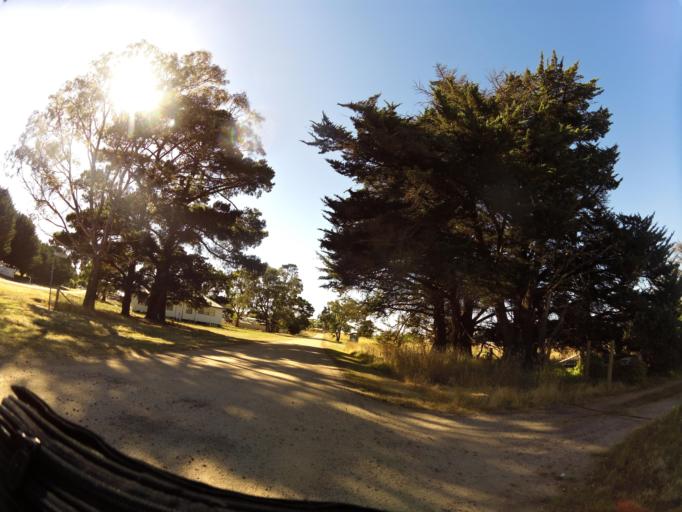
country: AU
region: Victoria
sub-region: Ballarat North
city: Delacombe
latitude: -37.6901
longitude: 143.3647
